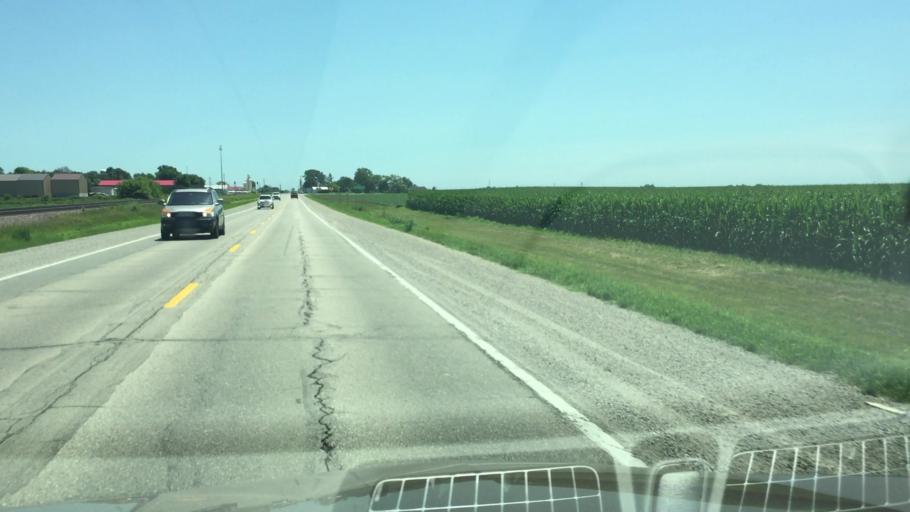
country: US
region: Iowa
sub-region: Cedar County
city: Mechanicsville
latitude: 41.9047
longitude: -91.2655
